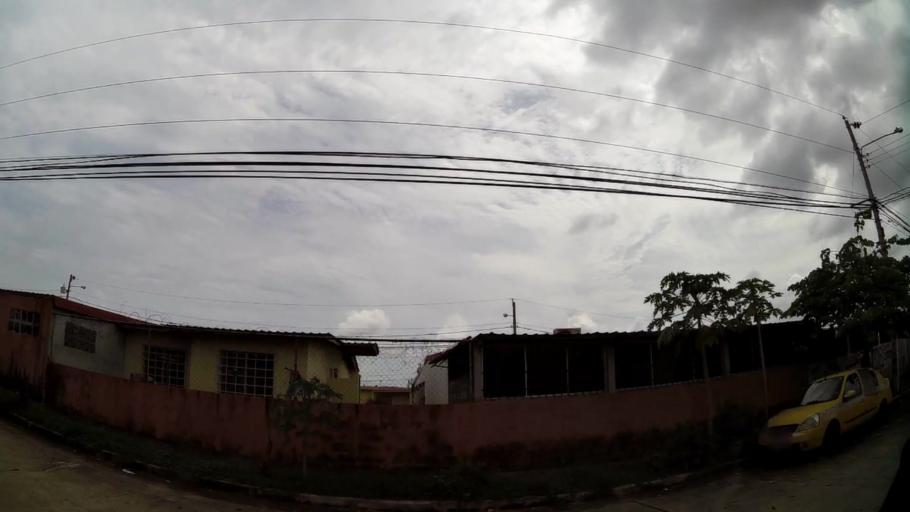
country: PA
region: Panama
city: San Miguelito
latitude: 9.0600
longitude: -79.4249
